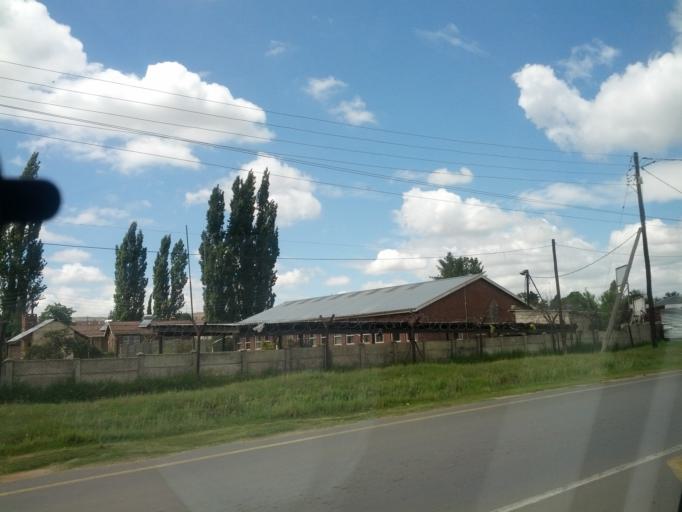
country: LS
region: Maseru
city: Maseru
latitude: -29.2842
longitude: 27.5271
